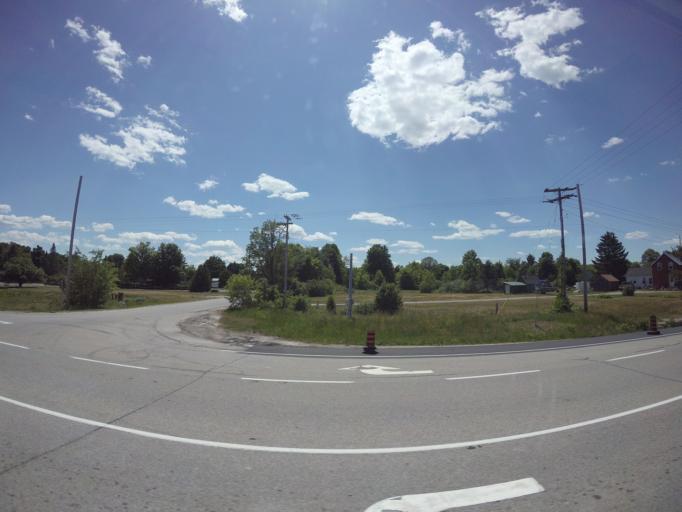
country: CA
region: Ontario
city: Carleton Place
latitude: 45.1305
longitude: -76.1702
